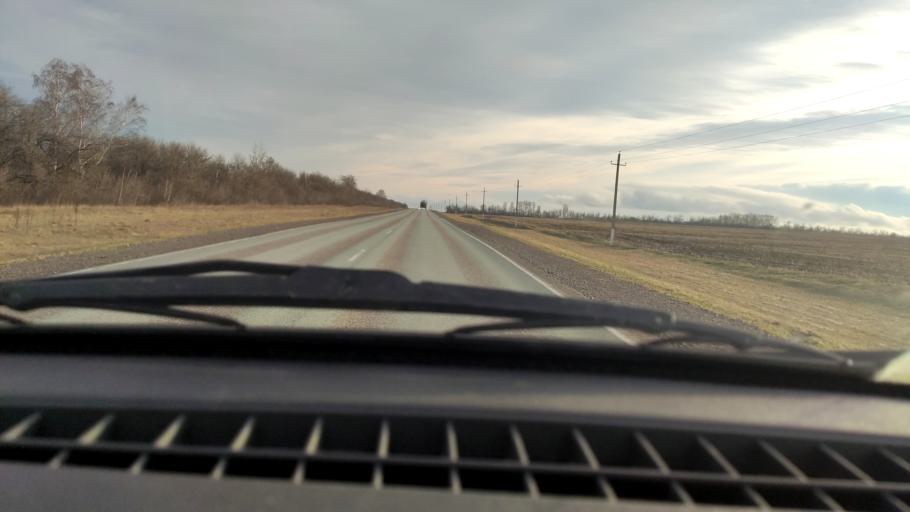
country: RU
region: Bashkortostan
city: Davlekanovo
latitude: 54.3241
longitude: 55.1593
